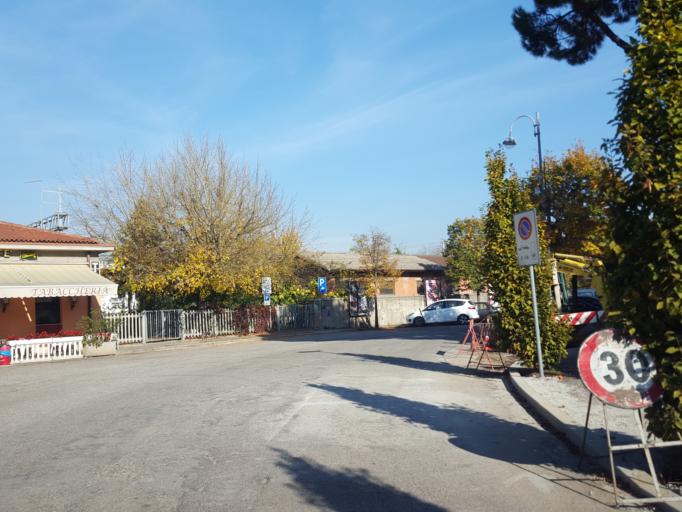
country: IT
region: Veneto
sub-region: Provincia di Verona
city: San Bonifacio
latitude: 45.4022
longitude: 11.2745
